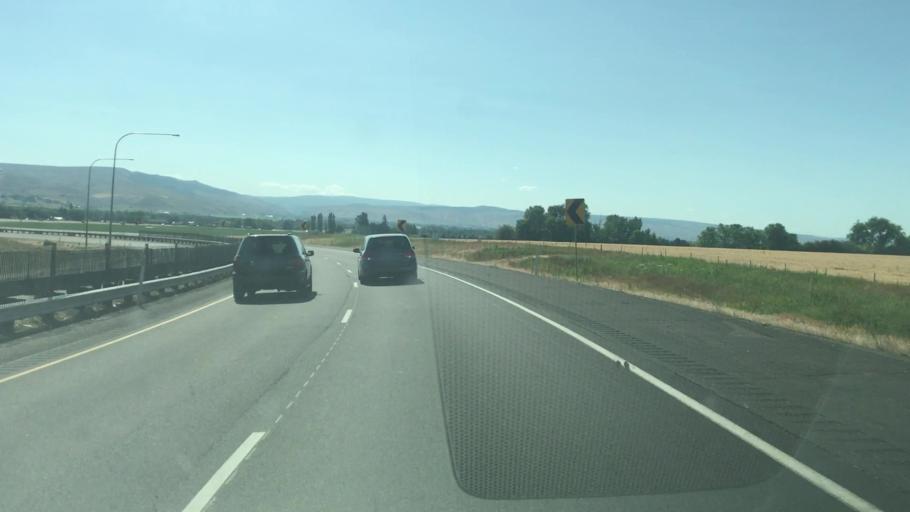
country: US
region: Washington
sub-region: Kittitas County
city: Ellensburg
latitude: 46.9731
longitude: -120.5149
